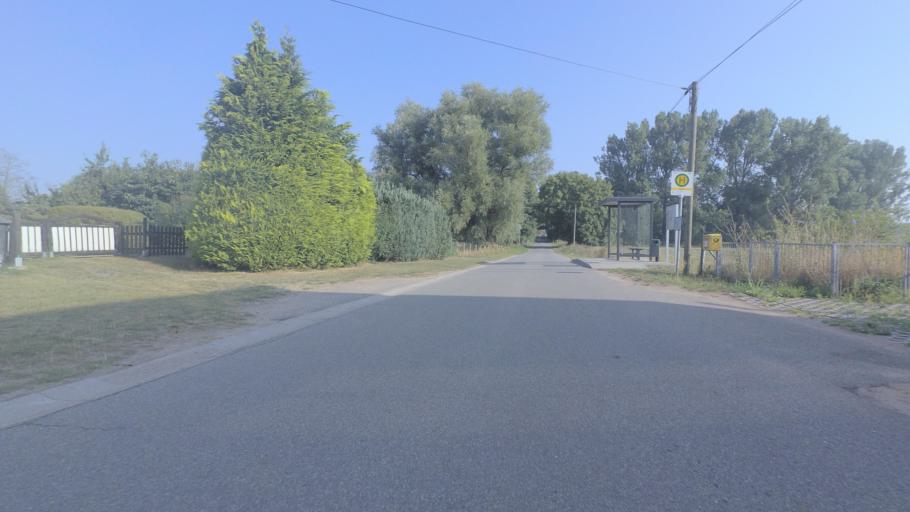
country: DE
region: Mecklenburg-Vorpommern
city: Malchow
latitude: 53.3578
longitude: 12.3811
